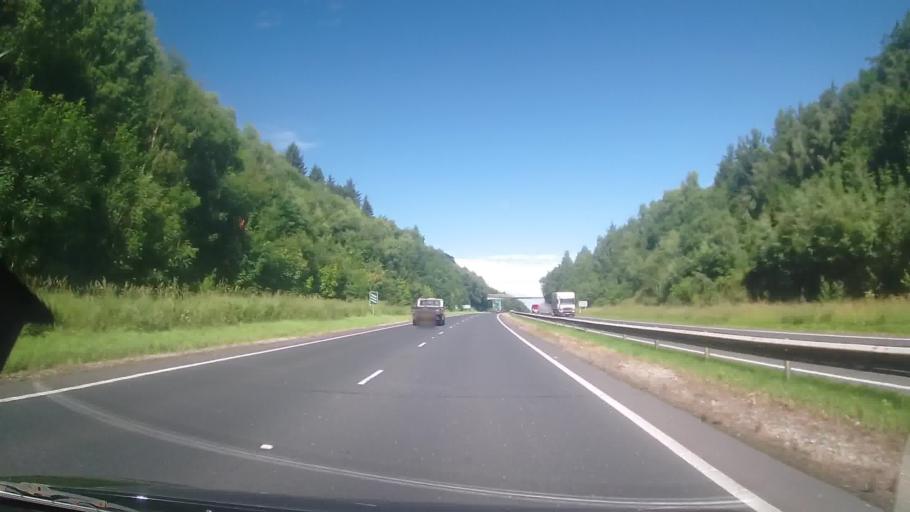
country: GB
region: Wales
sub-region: County of Flintshire
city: Hawarden
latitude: 53.1643
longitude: -3.0284
